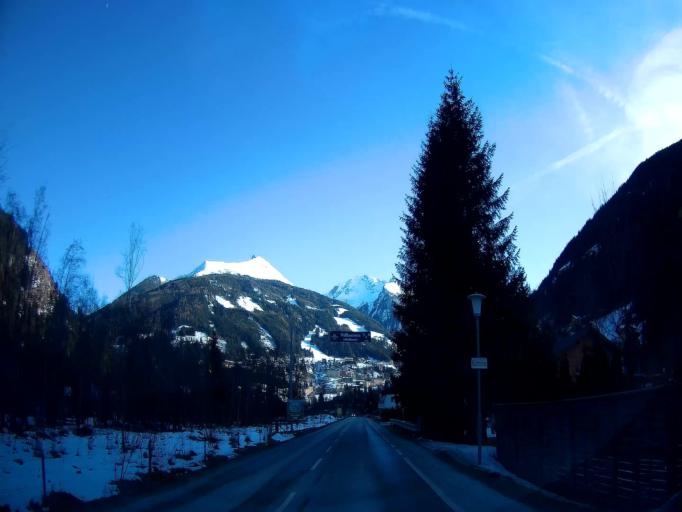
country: AT
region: Salzburg
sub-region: Politischer Bezirk Sankt Johann im Pongau
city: Bad Gastein
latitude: 47.1344
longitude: 13.1313
